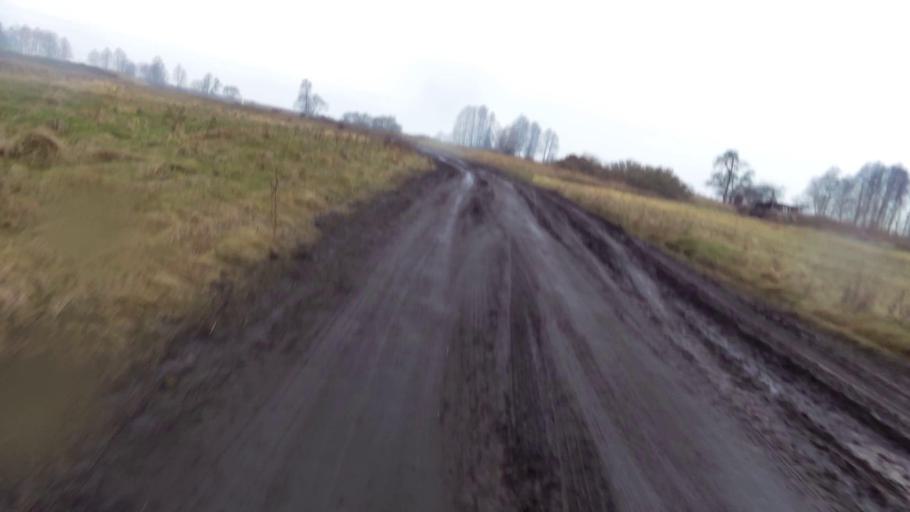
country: PL
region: West Pomeranian Voivodeship
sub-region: Szczecin
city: Szczecin
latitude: 53.4413
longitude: 14.7101
